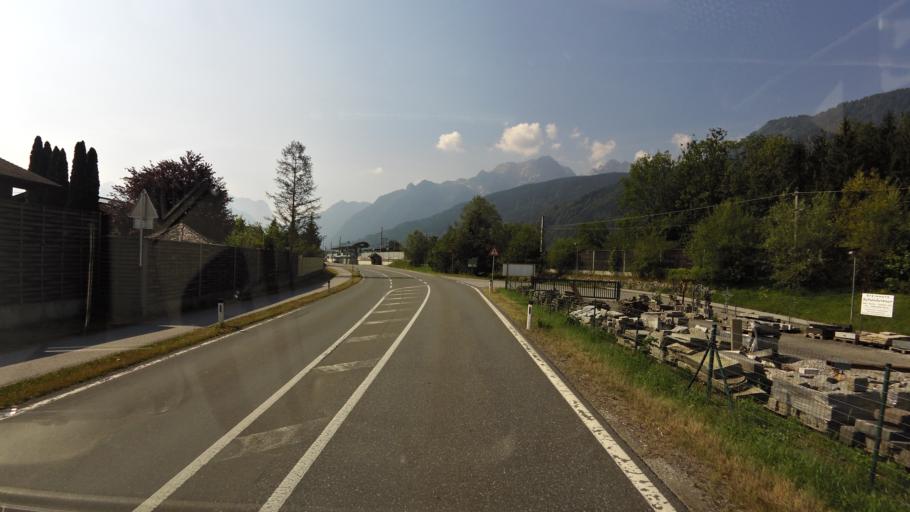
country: AT
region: Salzburg
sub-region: Politischer Bezirk Hallein
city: Adnet
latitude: 47.6535
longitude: 13.1281
